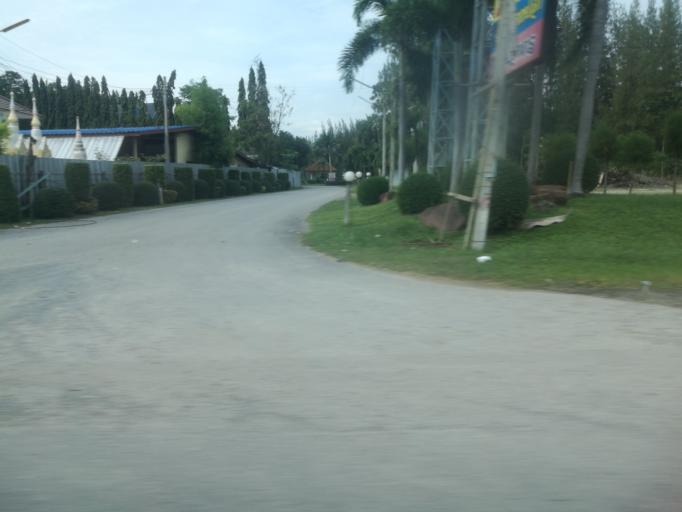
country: TH
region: Phetchaburi
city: Tha Yang
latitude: 12.8879
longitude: 99.9115
